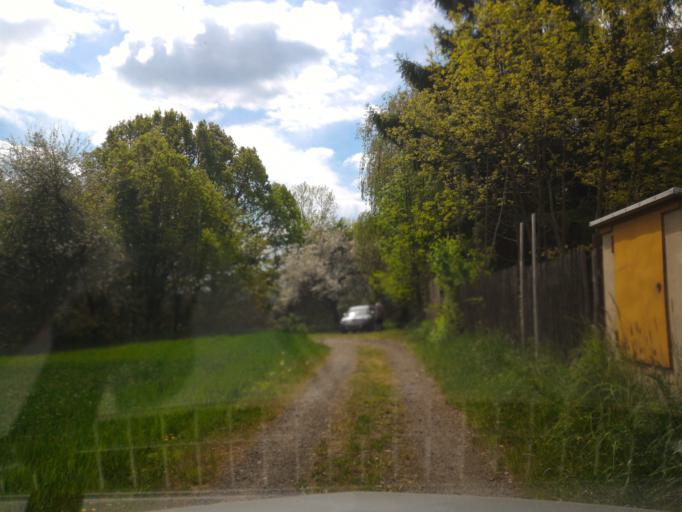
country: DE
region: Saxony
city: Seifhennersdorf
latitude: 50.9420
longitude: 14.6223
